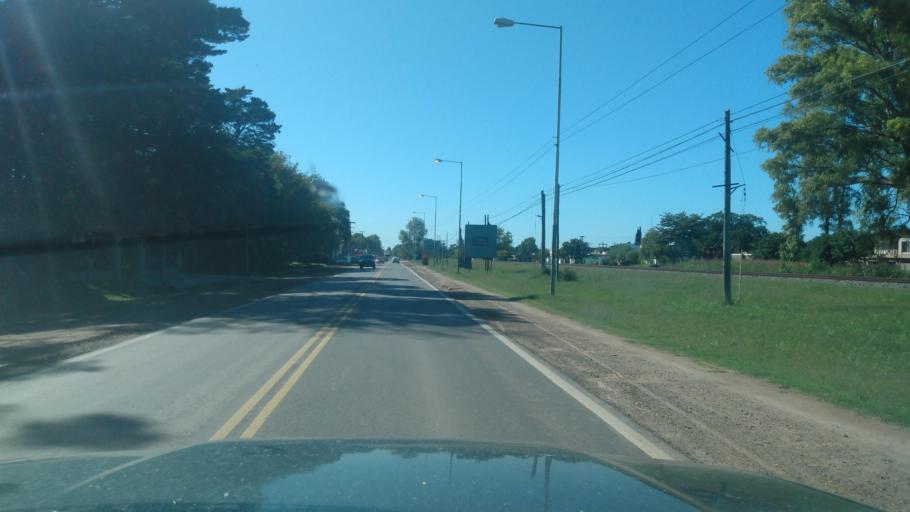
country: AR
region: Buenos Aires
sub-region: Partido de General Rodriguez
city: General Rodriguez
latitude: -34.6050
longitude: -58.9684
